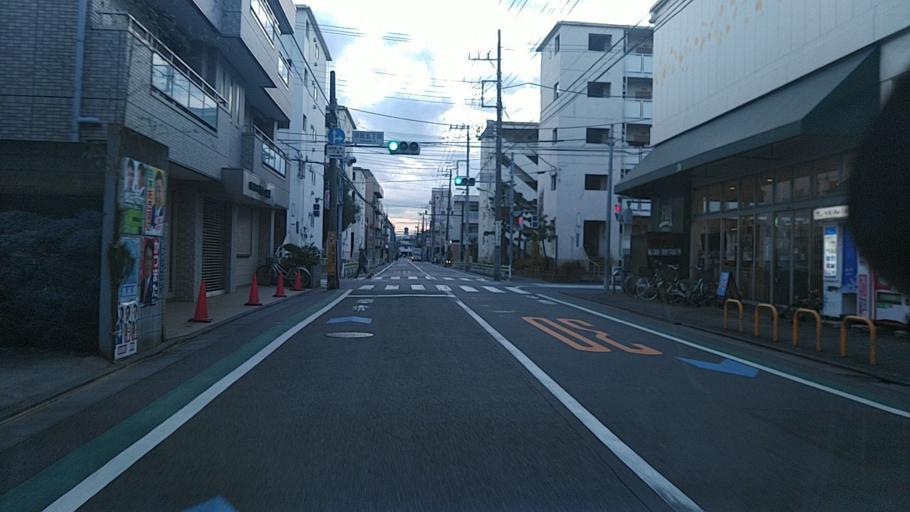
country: JP
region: Kanagawa
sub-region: Kawasaki-shi
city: Kawasaki
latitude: 35.5493
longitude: 139.7479
